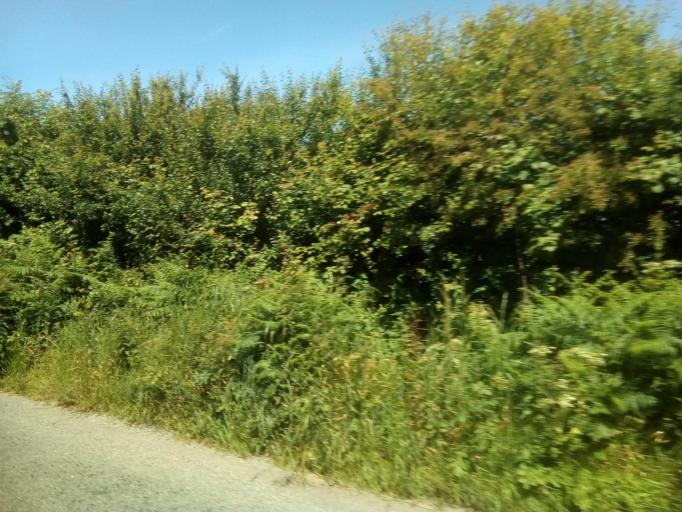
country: IE
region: Leinster
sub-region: Loch Garman
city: Loch Garman
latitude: 52.2346
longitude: -6.5756
